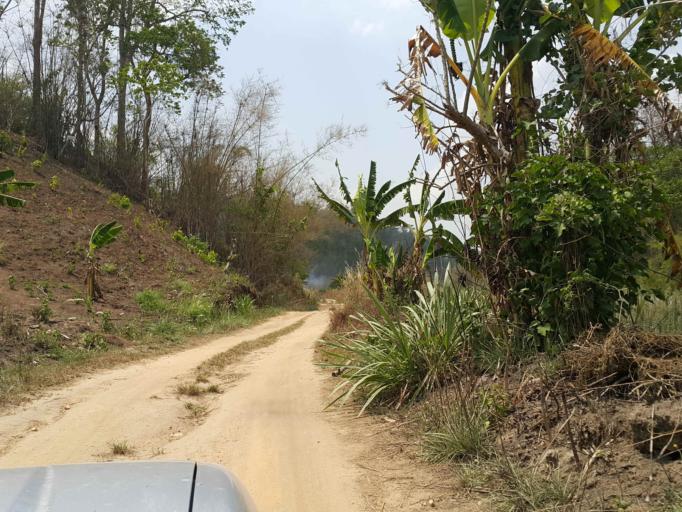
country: TH
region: Chiang Mai
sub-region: Amphoe Chiang Dao
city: Chiang Dao
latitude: 19.2779
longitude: 98.7656
